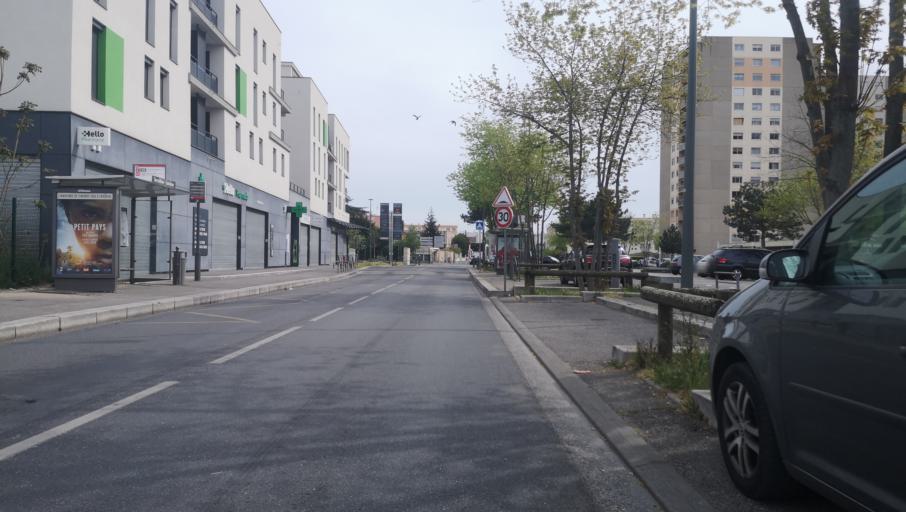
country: FR
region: Rhone-Alpes
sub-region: Departement du Rhone
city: Bron
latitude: 45.7438
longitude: 4.9194
